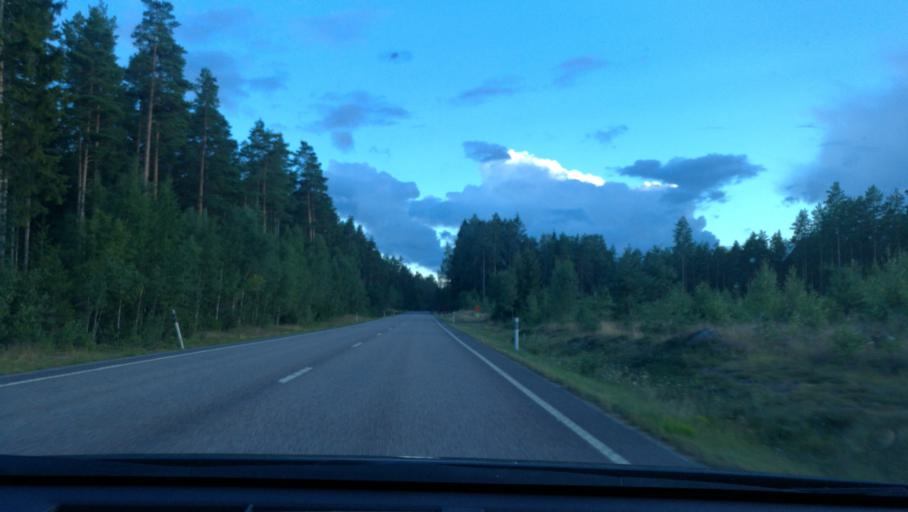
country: SE
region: Vaestmanland
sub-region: Kungsors Kommun
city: Kungsoer
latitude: 59.2229
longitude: 16.1023
